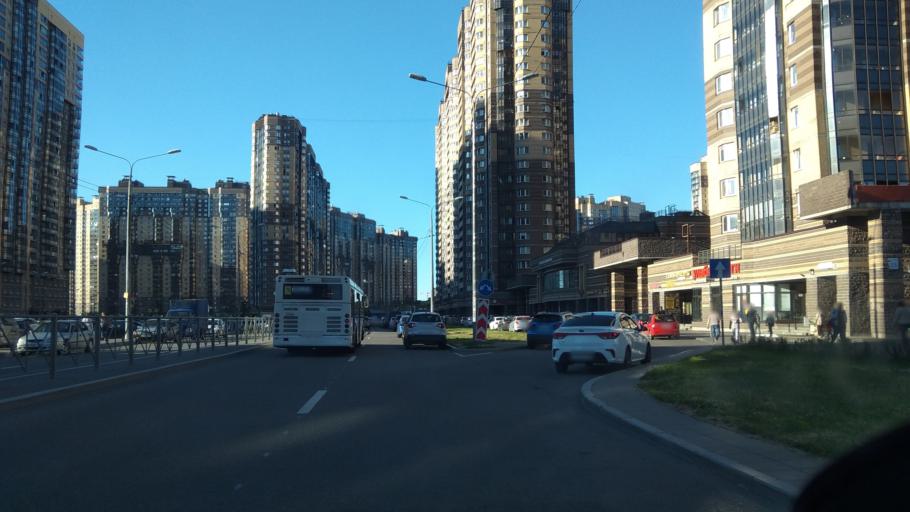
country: RU
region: Leningrad
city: Parnas
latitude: 60.0769
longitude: 30.3427
